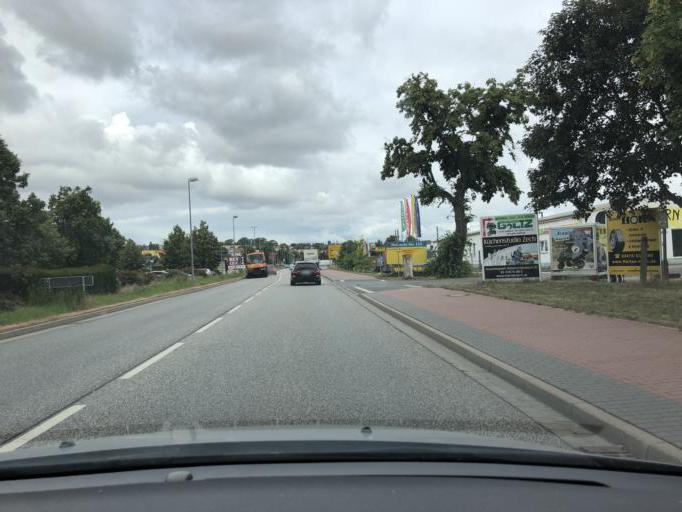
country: DE
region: Saxony-Anhalt
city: Volkstedt
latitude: 51.5098
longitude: 11.5798
